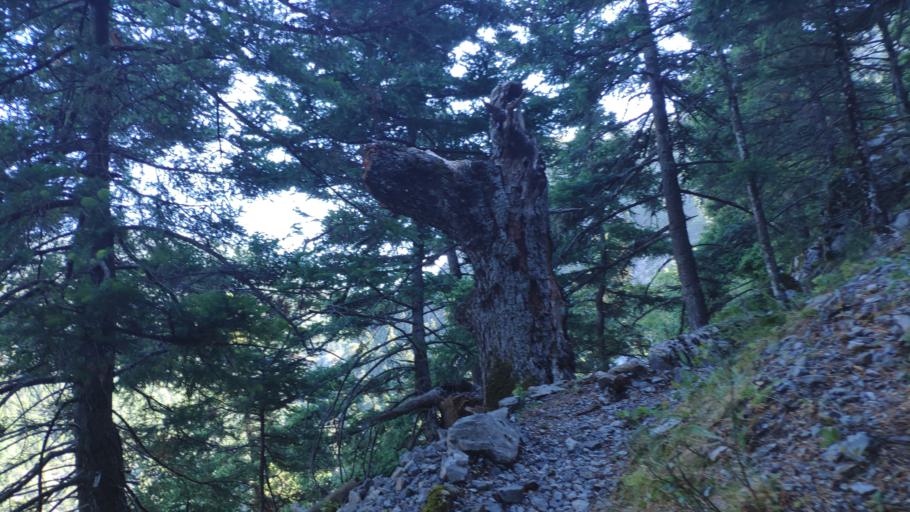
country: GR
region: Peloponnese
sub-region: Nomos Lakonias
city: Kariai
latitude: 37.1733
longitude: 22.6020
